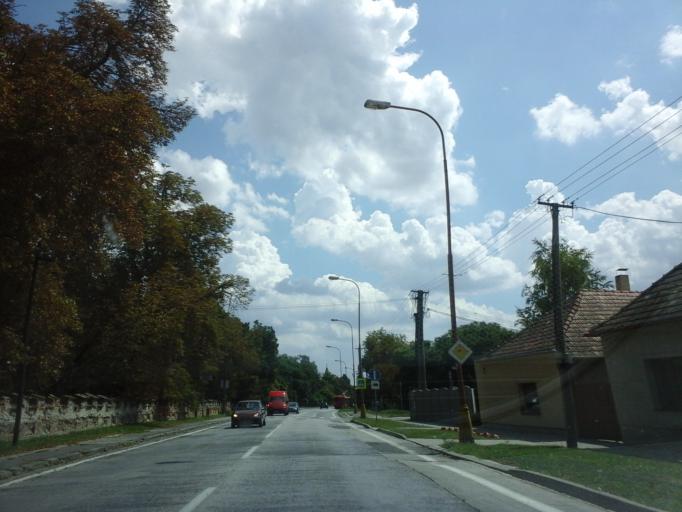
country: AT
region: Burgenland
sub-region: Politischer Bezirk Neusiedl am See
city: Deutsch Jahrndorf
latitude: 48.0519
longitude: 17.1494
